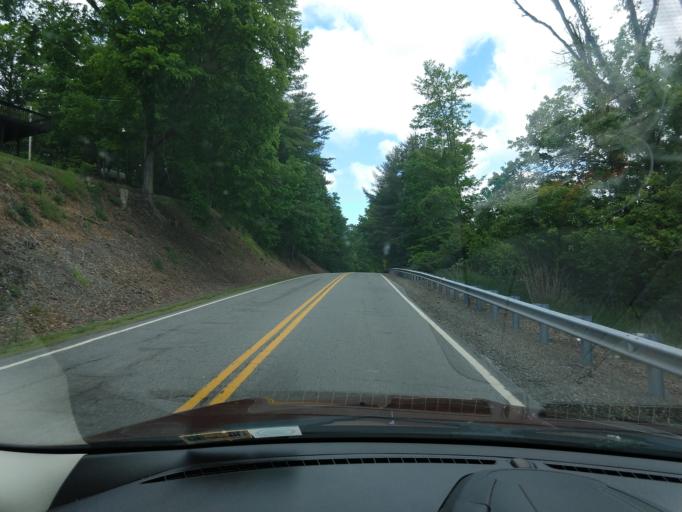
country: US
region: Virginia
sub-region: City of Galax
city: Galax
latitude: 36.7770
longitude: -80.9872
